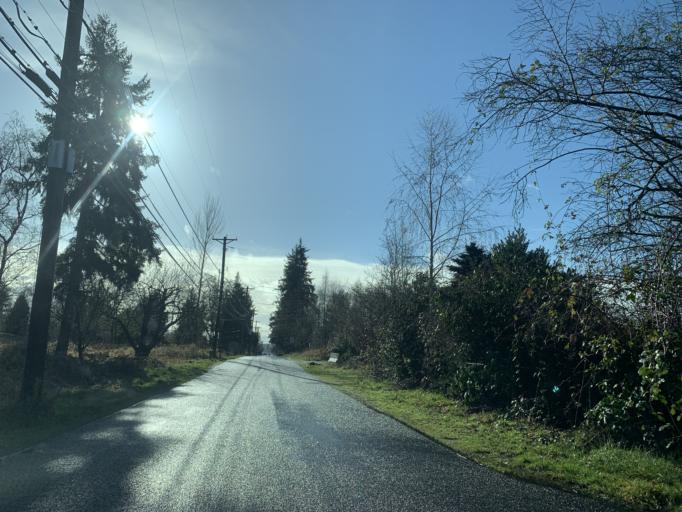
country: US
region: Washington
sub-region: Pierce County
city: Fife Heights
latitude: 47.2486
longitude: -122.3468
